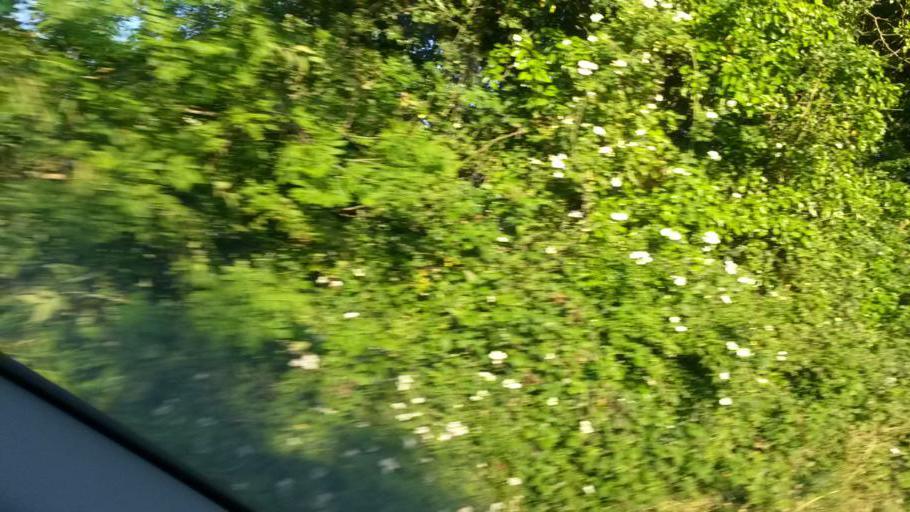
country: IE
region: Leinster
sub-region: An Mhi
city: Ashbourne
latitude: 53.5495
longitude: -6.3601
